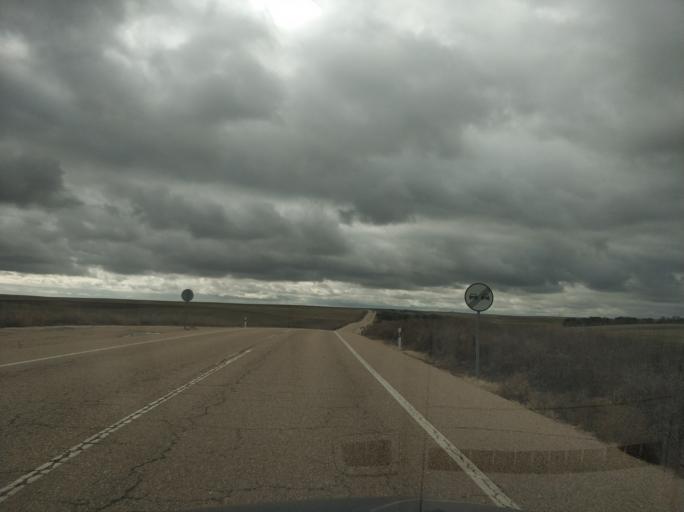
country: ES
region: Castille and Leon
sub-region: Provincia de Valladolid
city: Alaejos
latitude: 41.2687
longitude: -5.2598
